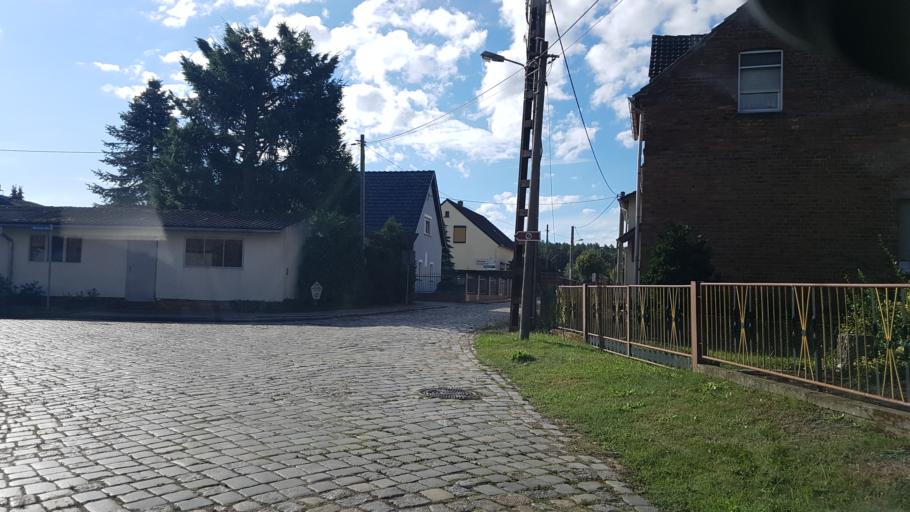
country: DE
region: Saxony
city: Gross Duben
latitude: 51.6217
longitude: 14.5369
